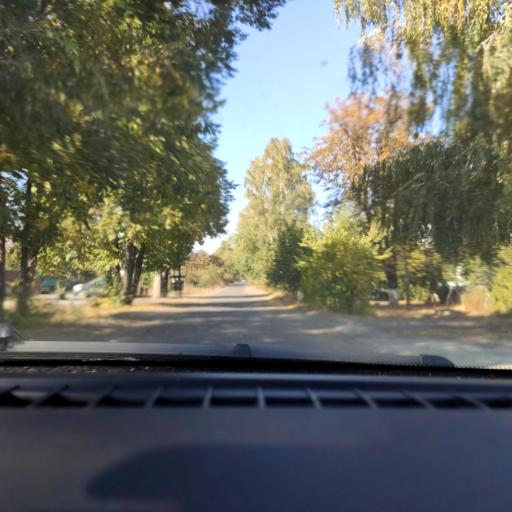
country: RU
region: Voronezj
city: Maslovka
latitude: 51.6160
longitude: 39.2649
